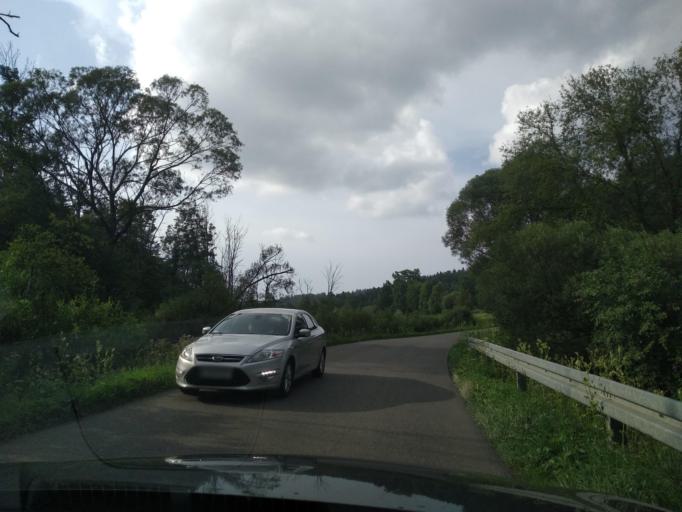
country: PL
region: Subcarpathian Voivodeship
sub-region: Powiat leski
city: Olszanica
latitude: 49.5123
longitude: 22.4638
